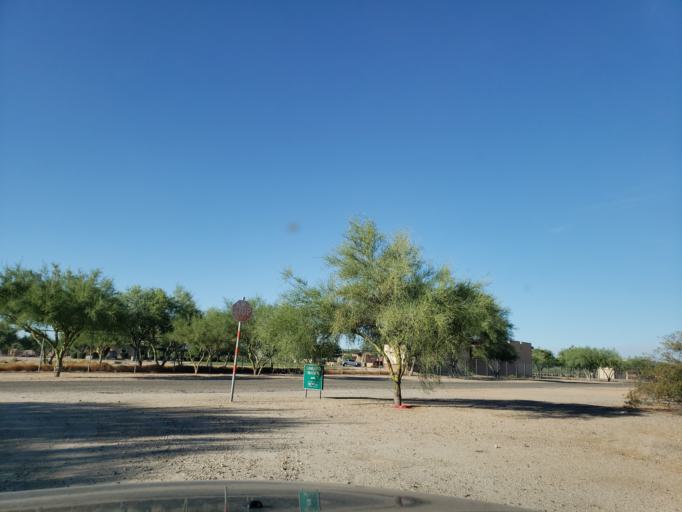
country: US
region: Arizona
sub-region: Maricopa County
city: Cave Creek
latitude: 33.6942
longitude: -112.0284
